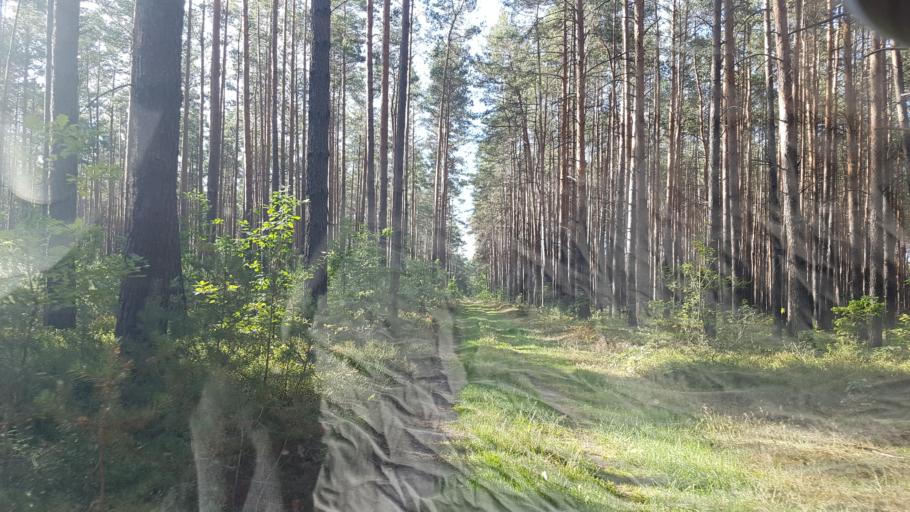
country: DE
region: Brandenburg
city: Finsterwalde
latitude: 51.5843
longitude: 13.6557
